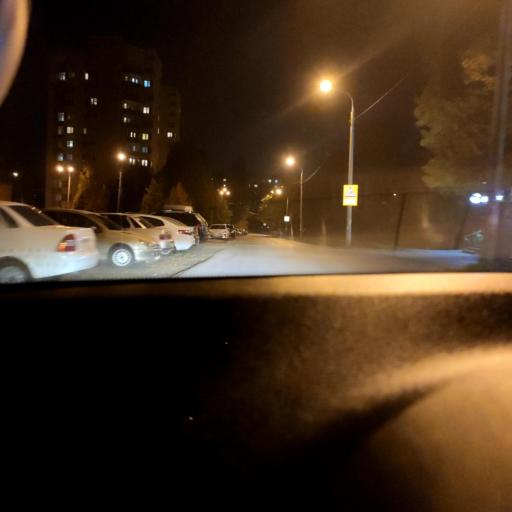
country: RU
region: Samara
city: Samara
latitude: 53.2565
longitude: 50.2406
